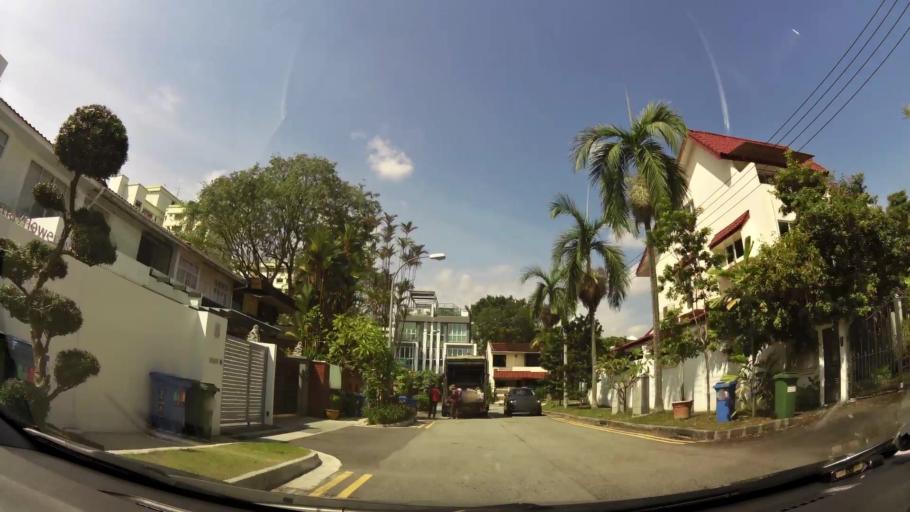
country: SG
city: Singapore
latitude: 1.3721
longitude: 103.8398
